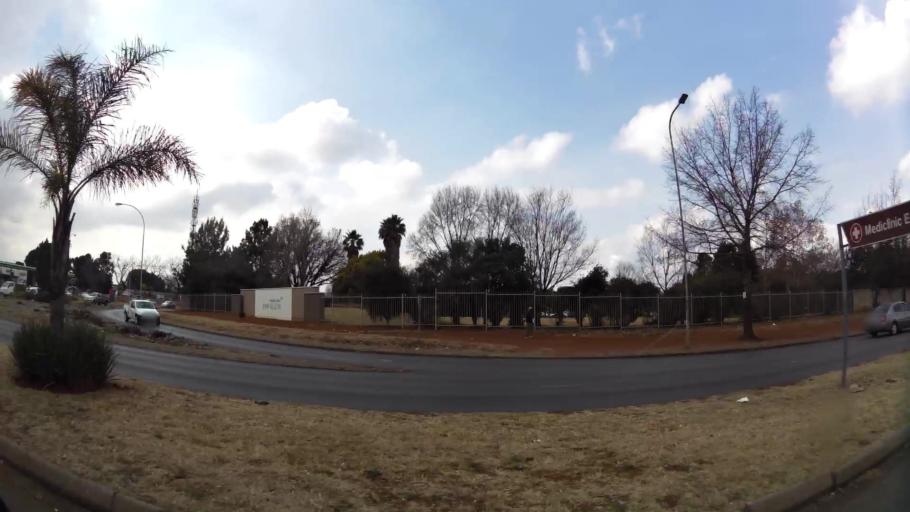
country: ZA
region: Gauteng
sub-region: Sedibeng District Municipality
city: Vanderbijlpark
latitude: -26.7038
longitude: 27.8355
